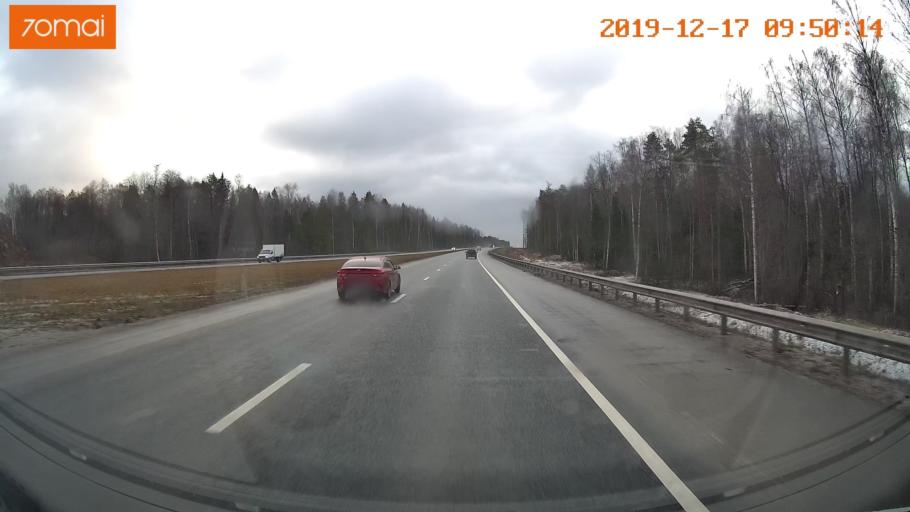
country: RU
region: Vladimir
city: Kommunar
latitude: 56.0605
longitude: 40.5069
